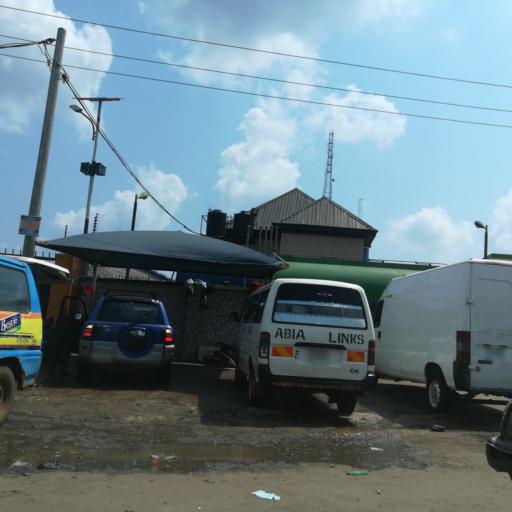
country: NG
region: Rivers
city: Port Harcourt
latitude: 4.8582
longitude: 7.0672
